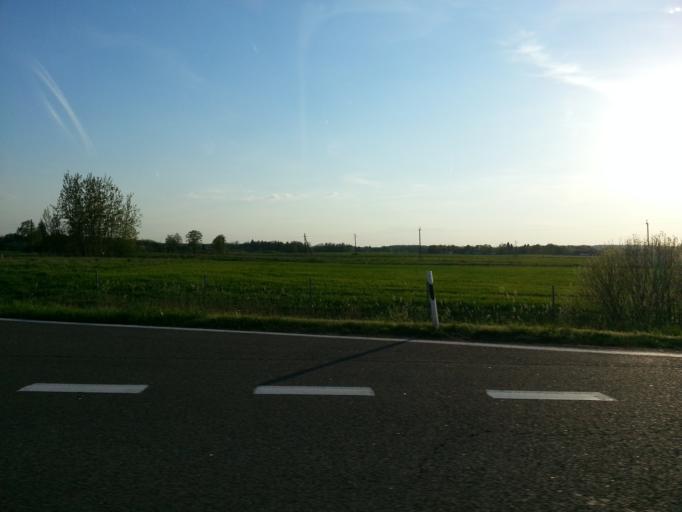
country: LT
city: Sirvintos
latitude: 55.0682
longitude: 24.8841
